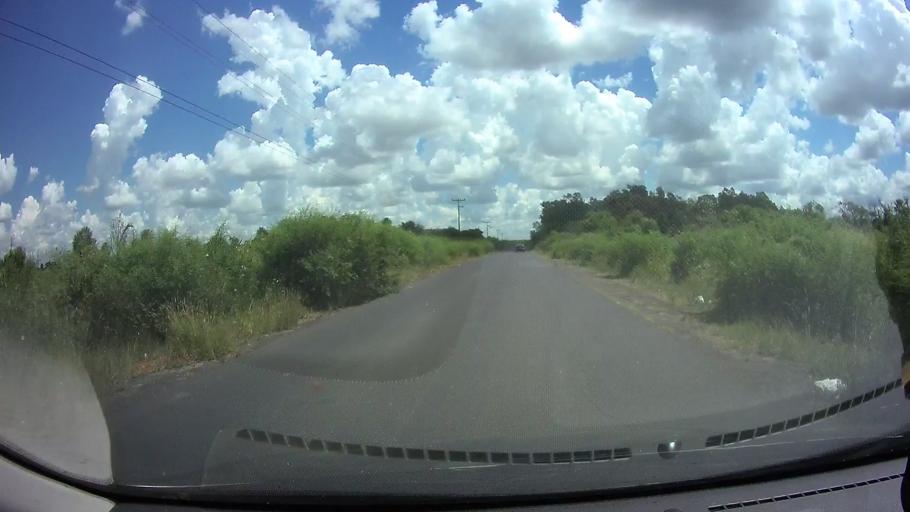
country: PY
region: Presidente Hayes
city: Nanawa
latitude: -25.2453
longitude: -57.6679
